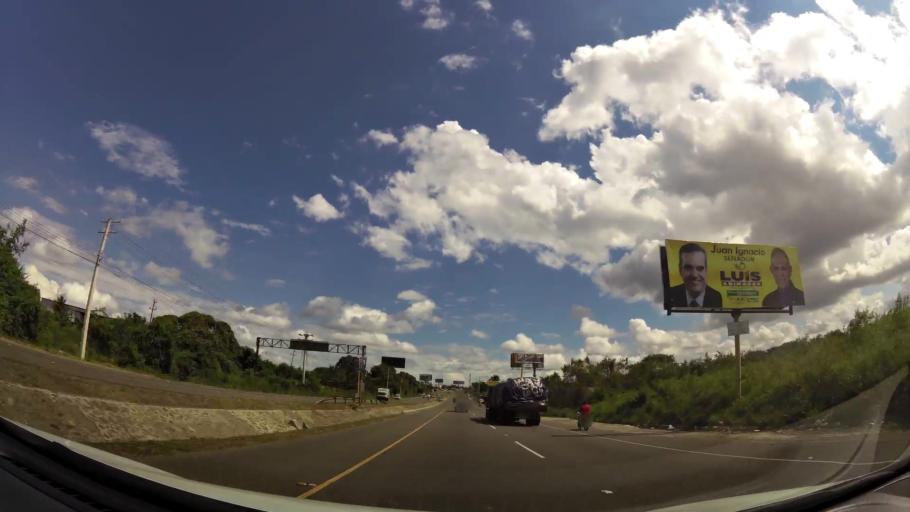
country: DO
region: Santiago
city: Licey al Medio
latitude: 19.3796
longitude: -70.6101
